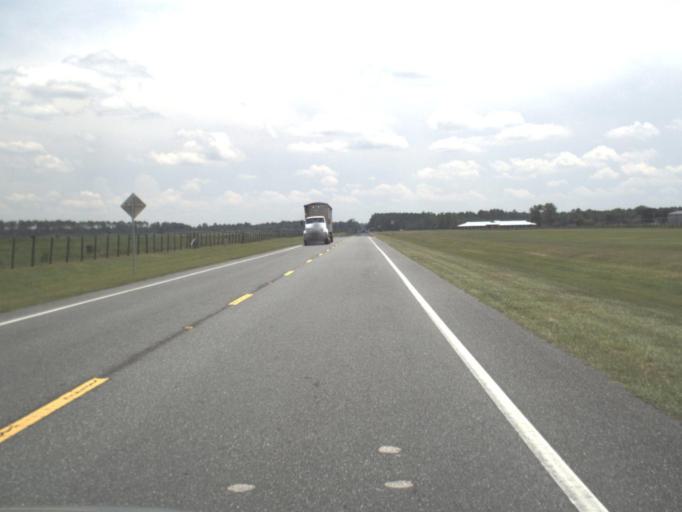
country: US
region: Florida
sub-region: Bradford County
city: Starke
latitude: 30.0563
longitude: -82.1768
